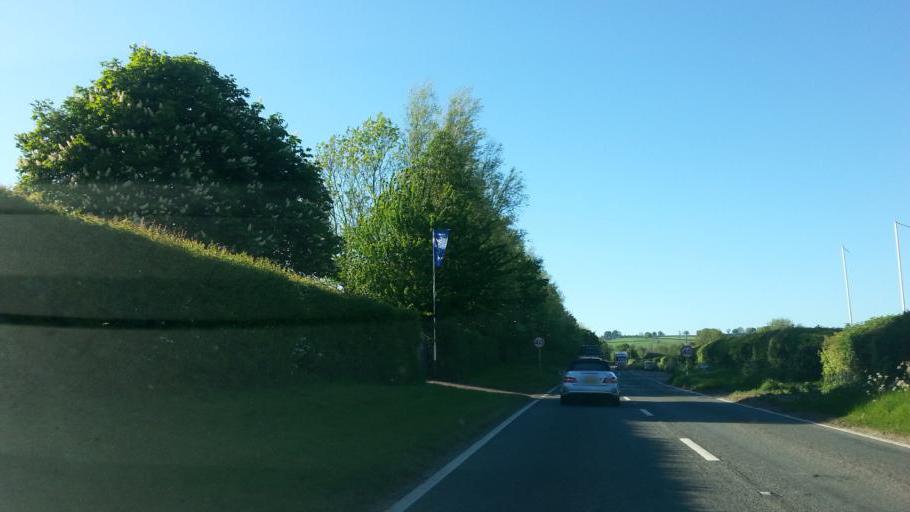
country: GB
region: England
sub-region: Somerset
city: Evercreech
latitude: 51.1535
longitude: -2.5220
